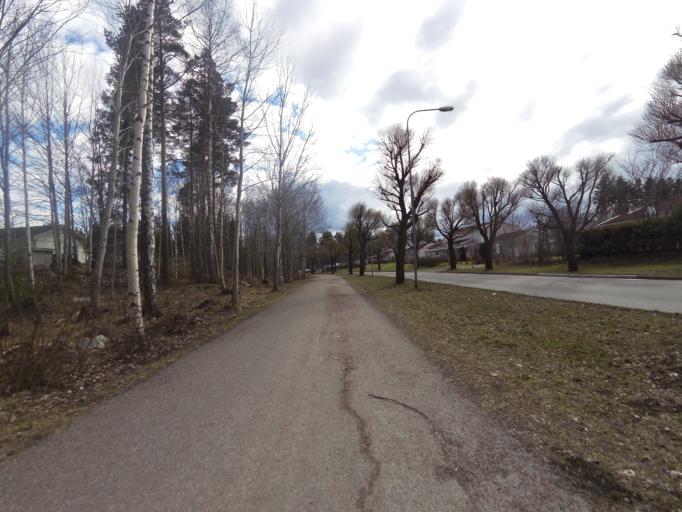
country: SE
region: Gaevleborg
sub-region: Gavle Kommun
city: Gavle
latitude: 60.6971
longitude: 17.0911
